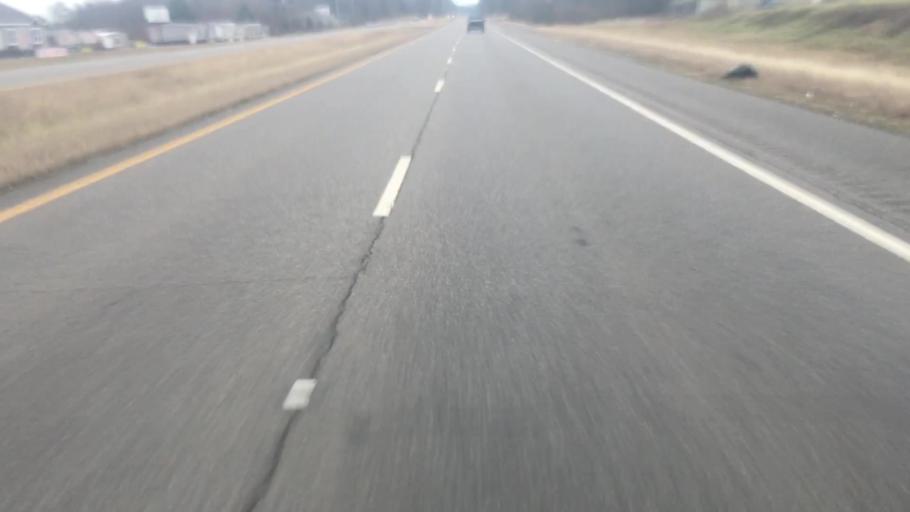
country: US
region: Alabama
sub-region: Walker County
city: Jasper
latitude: 33.8306
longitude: -87.2100
